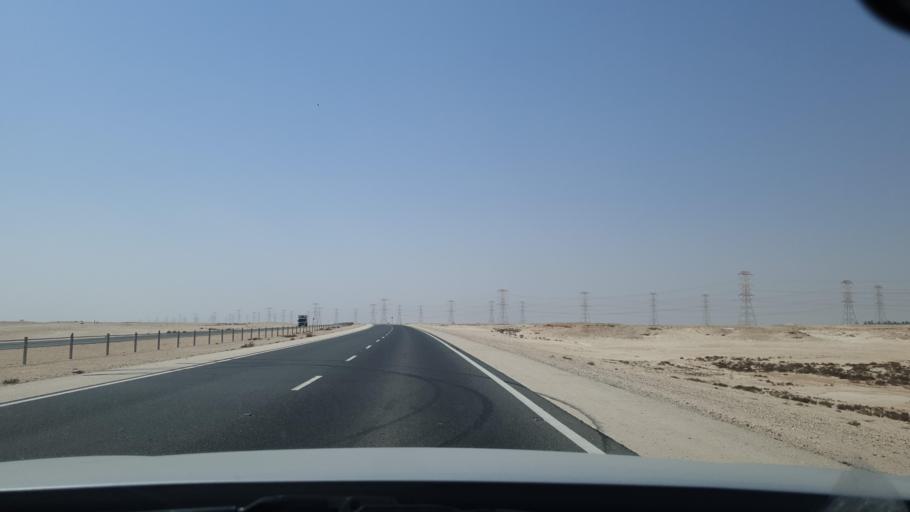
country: QA
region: Al Khawr
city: Al Khawr
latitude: 25.7500
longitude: 51.4688
